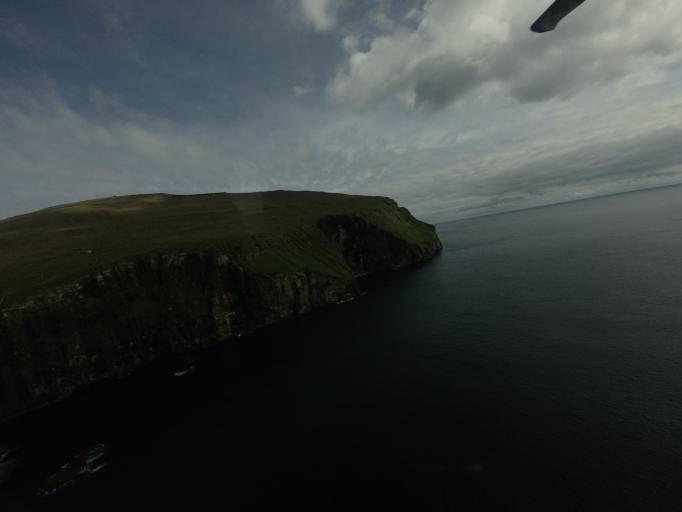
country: FO
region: Nordoyar
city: Klaksvik
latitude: 62.3145
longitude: -6.3079
